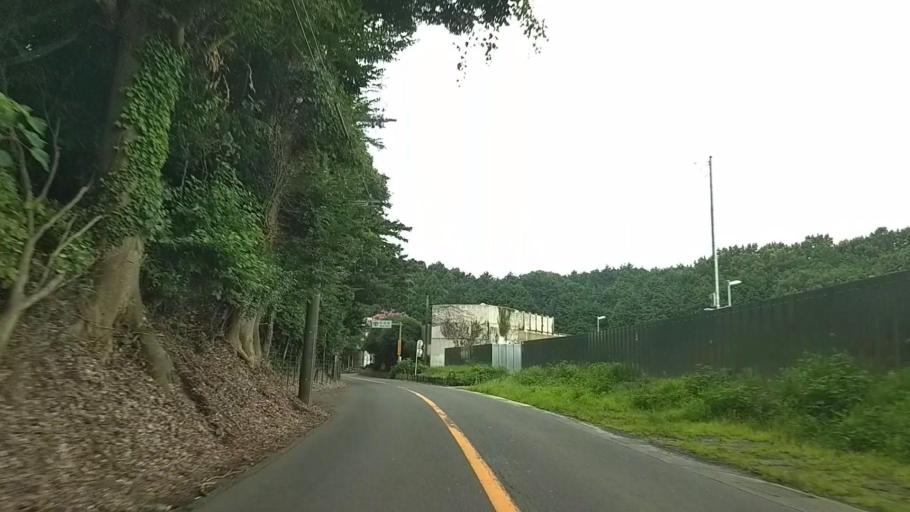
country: JP
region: Kanagawa
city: Ninomiya
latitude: 35.3357
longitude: 139.2408
